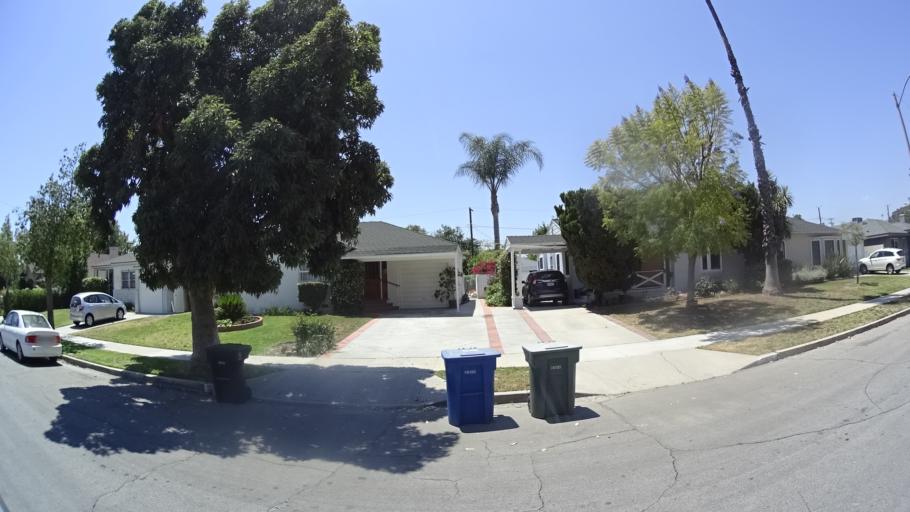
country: US
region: California
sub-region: Los Angeles County
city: North Hollywood
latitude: 34.1832
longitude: -118.3448
